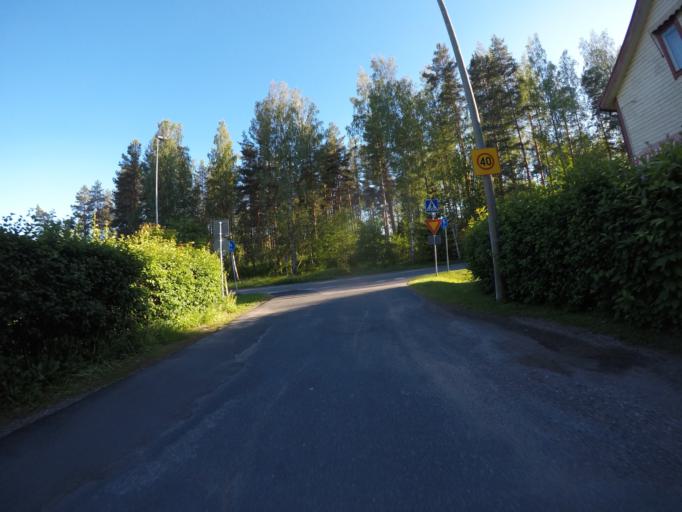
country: FI
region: Haeme
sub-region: Haemeenlinna
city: Haemeenlinna
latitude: 60.9825
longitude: 24.4527
